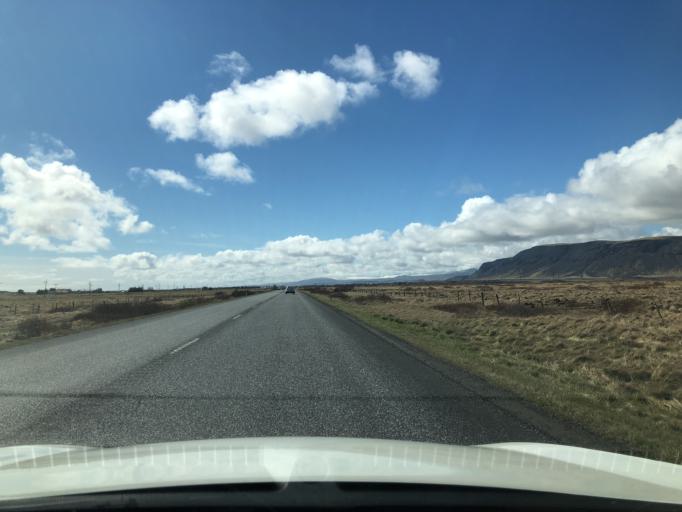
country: IS
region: South
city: Selfoss
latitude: 63.9423
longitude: -20.9049
